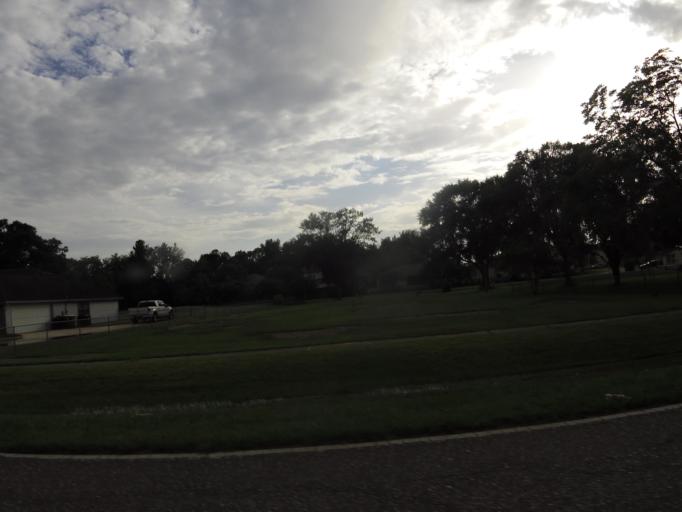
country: US
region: Florida
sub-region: Nassau County
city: Nassau Village-Ratliff
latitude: 30.4215
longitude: -81.7629
